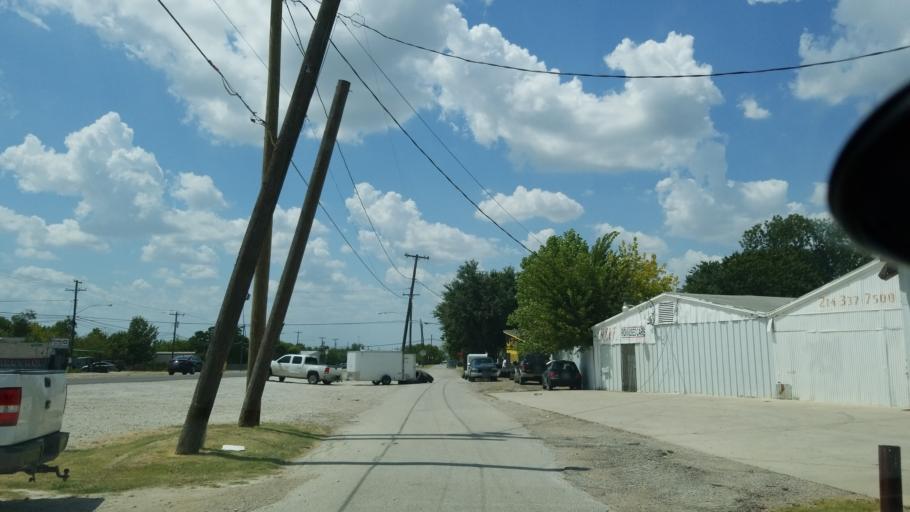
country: US
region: Texas
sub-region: Dallas County
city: Cockrell Hill
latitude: 32.7444
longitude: -96.9065
